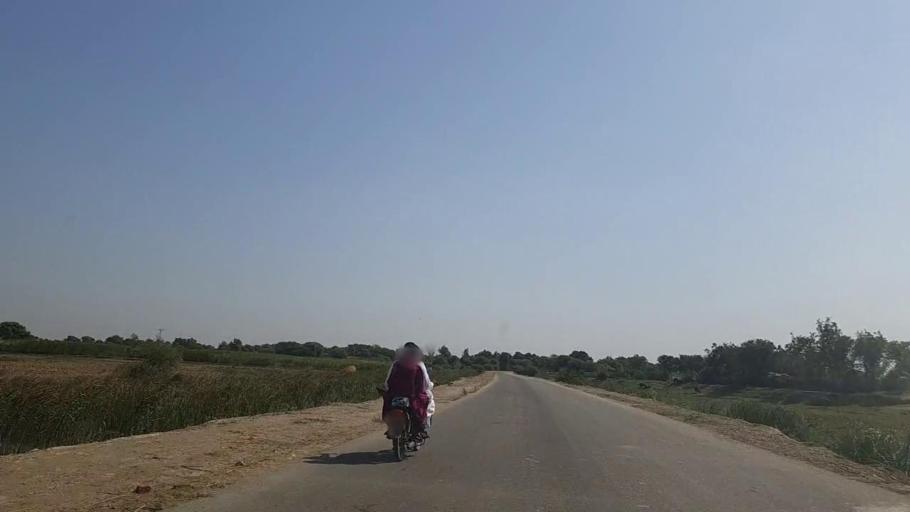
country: PK
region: Sindh
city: Daro Mehar
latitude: 24.7660
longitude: 68.2156
